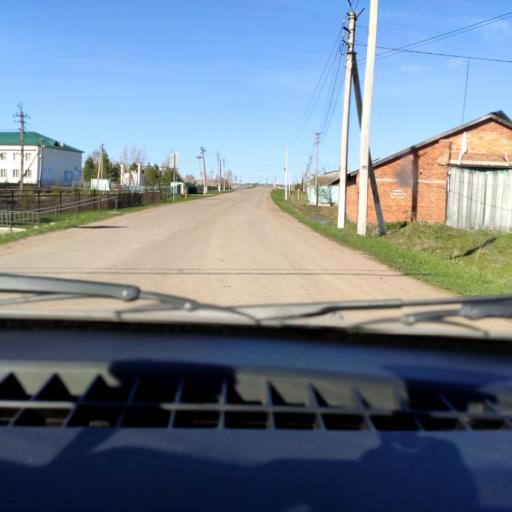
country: RU
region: Bashkortostan
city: Kabakovo
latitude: 54.5955
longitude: 56.1798
